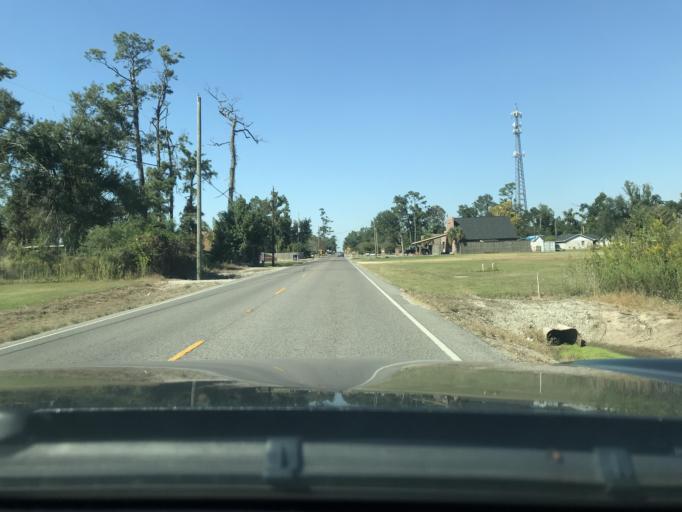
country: US
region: Louisiana
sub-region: Calcasieu Parish
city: Moss Bluff
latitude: 30.3083
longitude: -93.2001
